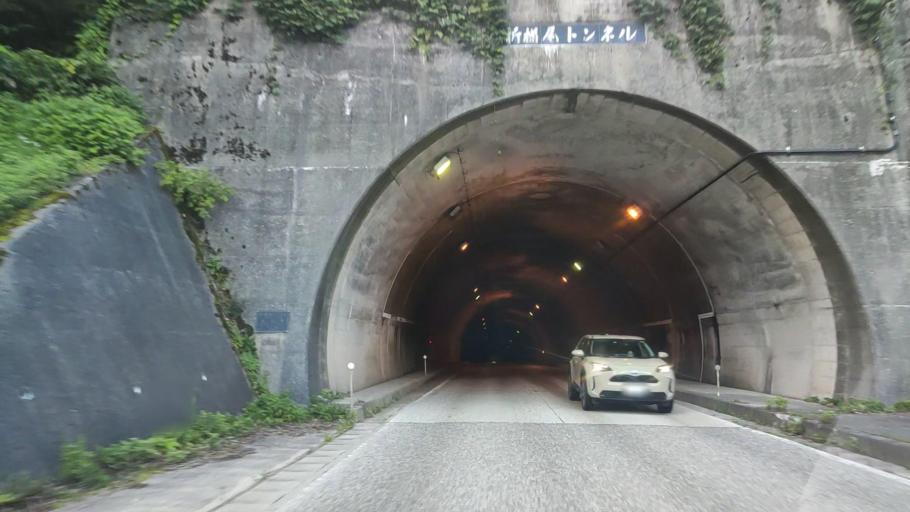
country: JP
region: Toyama
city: Yatsuomachi-higashikumisaka
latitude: 36.4526
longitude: 137.0398
